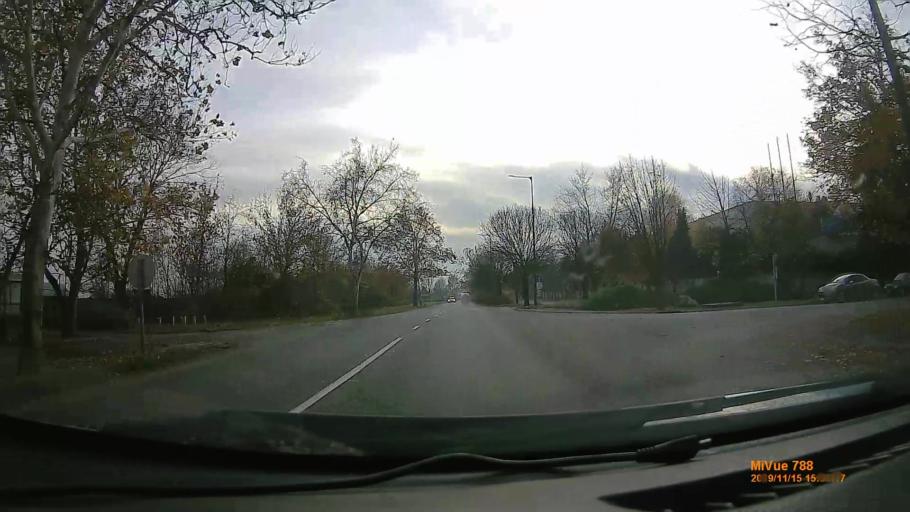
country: HU
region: Bekes
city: Gyula
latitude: 46.6387
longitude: 21.2624
